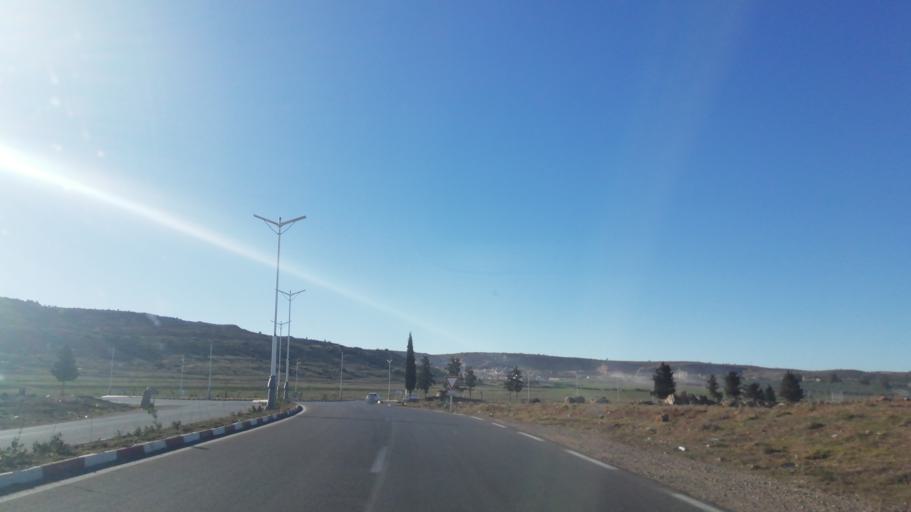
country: DZ
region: Saida
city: Saida
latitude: 34.8537
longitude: 0.1965
